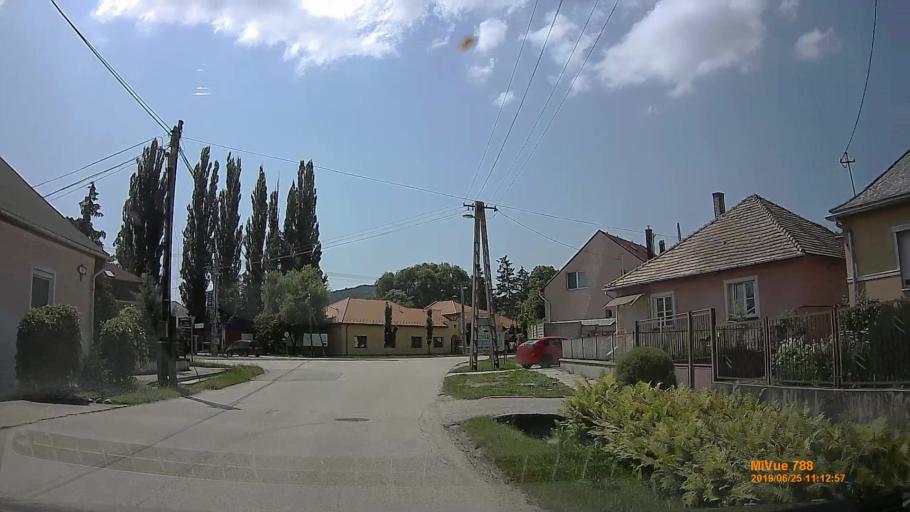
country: HU
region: Komarom-Esztergom
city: Tokod
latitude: 47.7232
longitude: 18.6580
